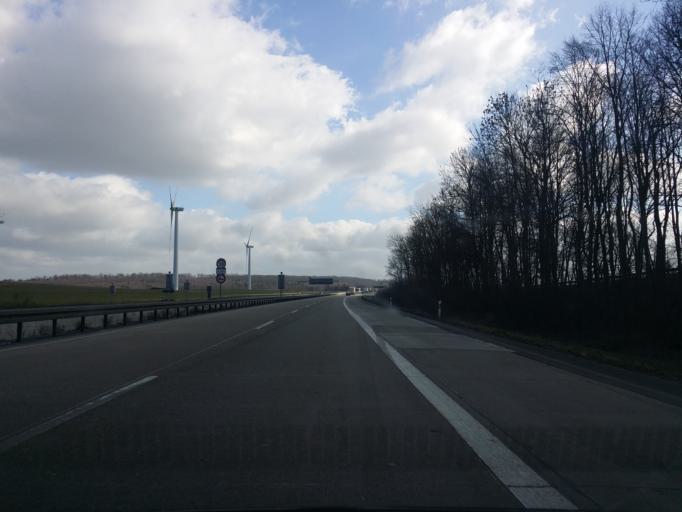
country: DE
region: Lower Saxony
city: Holle
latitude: 52.0856
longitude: 10.1825
